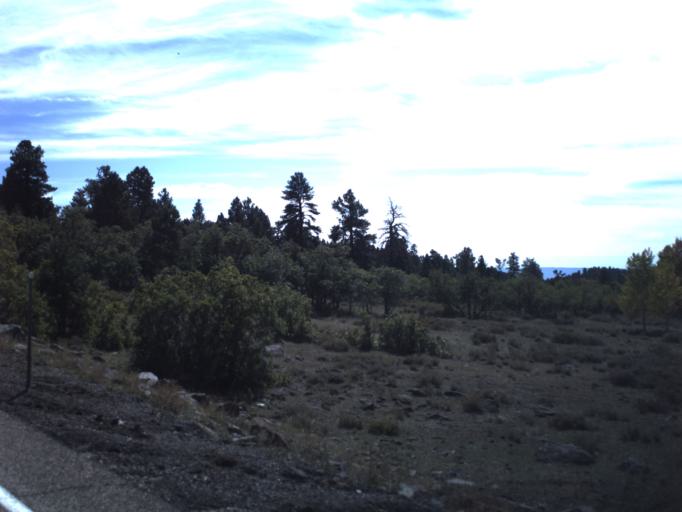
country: US
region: Utah
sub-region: Wayne County
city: Loa
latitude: 38.0080
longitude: -111.3962
